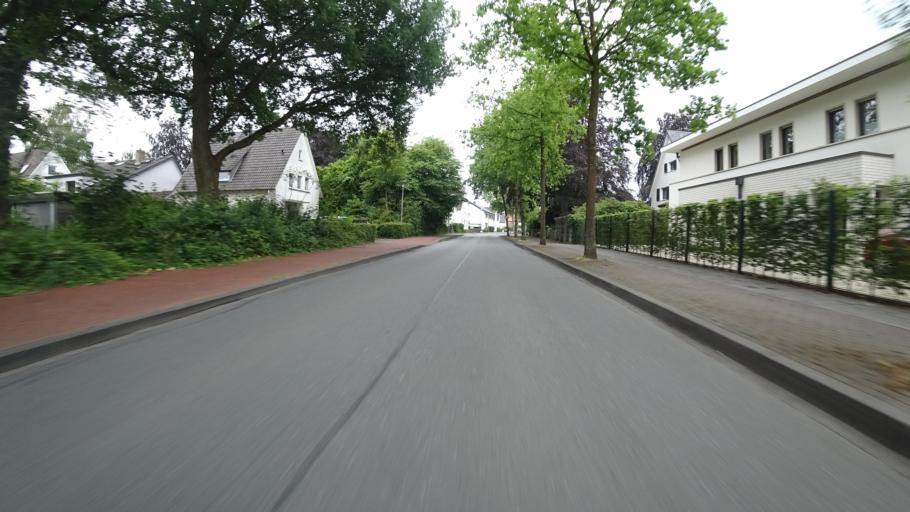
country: DE
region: North Rhine-Westphalia
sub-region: Regierungsbezirk Detmold
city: Guetersloh
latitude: 51.9303
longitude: 8.3842
